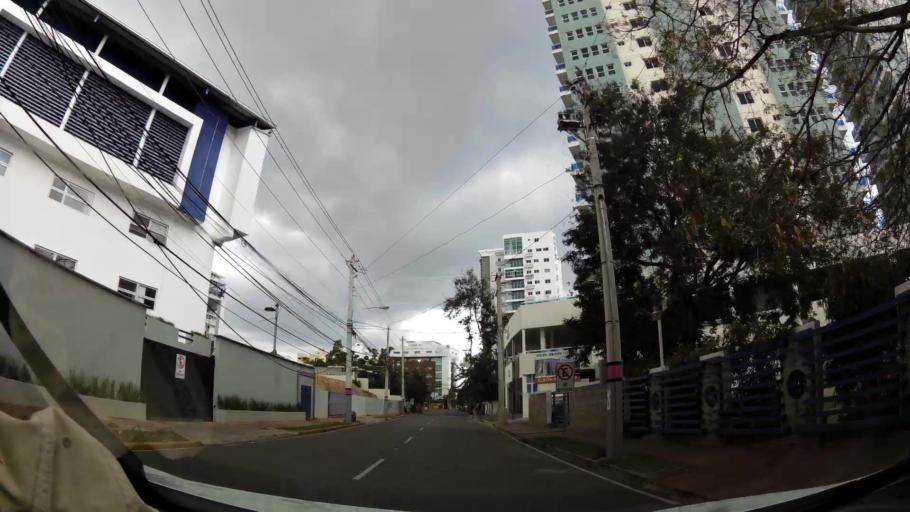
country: DO
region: Nacional
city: Ciudad Nueva
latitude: 18.4704
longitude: -69.9165
